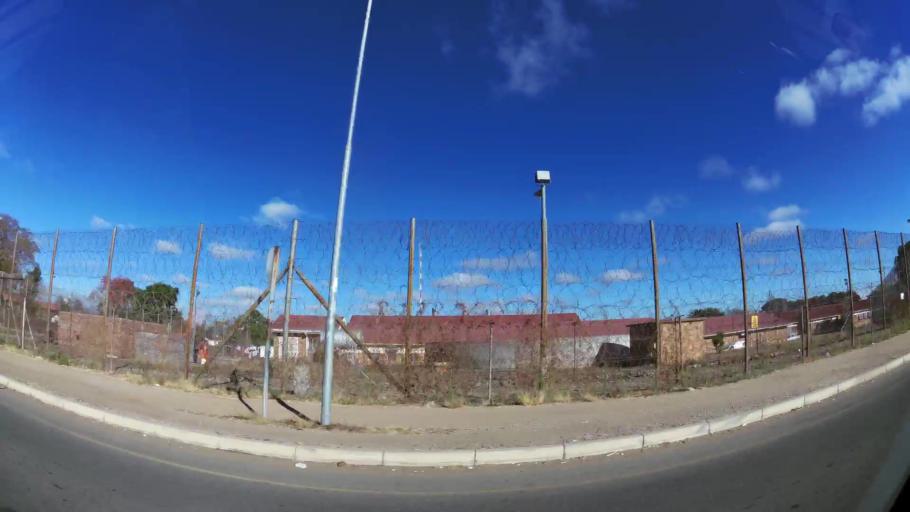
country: ZA
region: Limpopo
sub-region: Capricorn District Municipality
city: Polokwane
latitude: -23.8965
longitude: 29.4533
